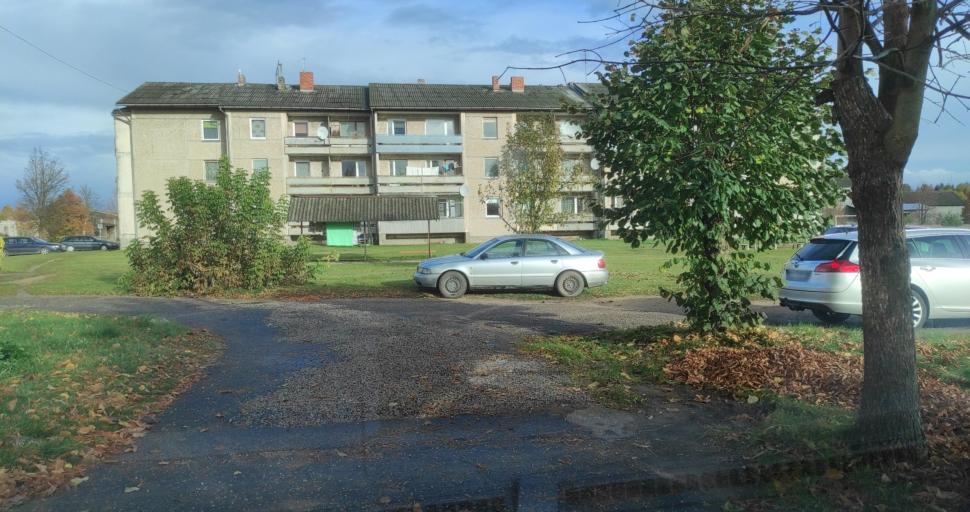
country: LV
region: Skrunda
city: Skrunda
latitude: 56.6832
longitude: 22.0492
